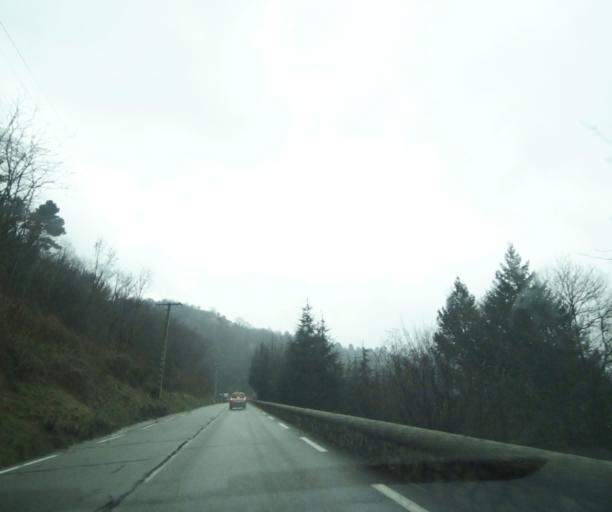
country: FR
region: Rhone-Alpes
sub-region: Departement de l'Ardeche
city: Thueyts
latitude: 44.6770
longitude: 4.2329
